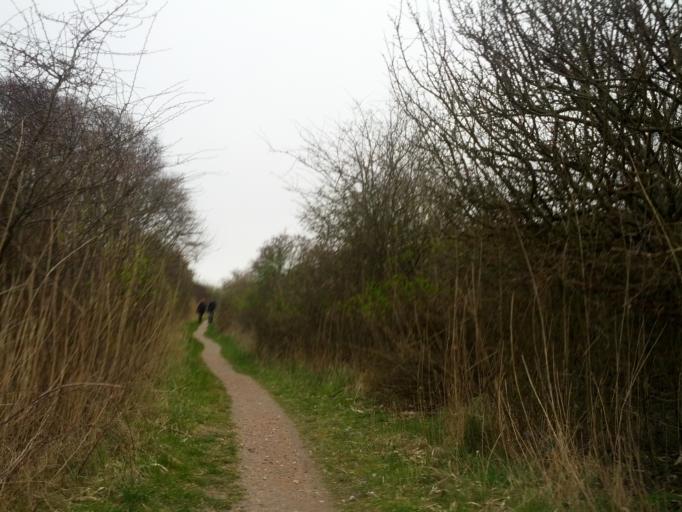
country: DE
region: Lower Saxony
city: Langeoog
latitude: 53.7395
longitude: 7.4718
